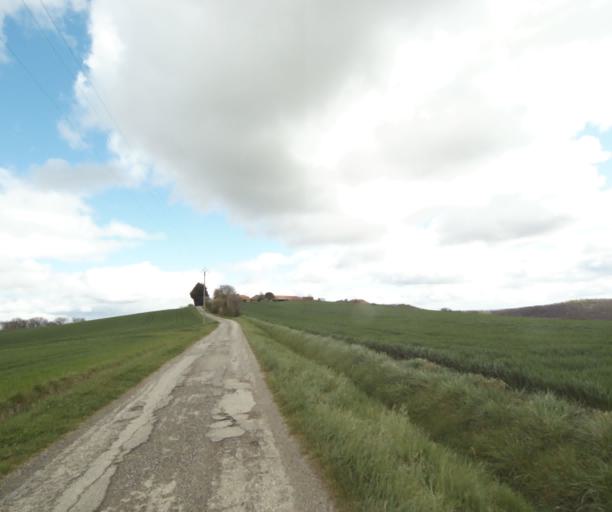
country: FR
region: Midi-Pyrenees
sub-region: Departement de l'Ariege
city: Saverdun
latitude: 43.1965
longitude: 1.5507
